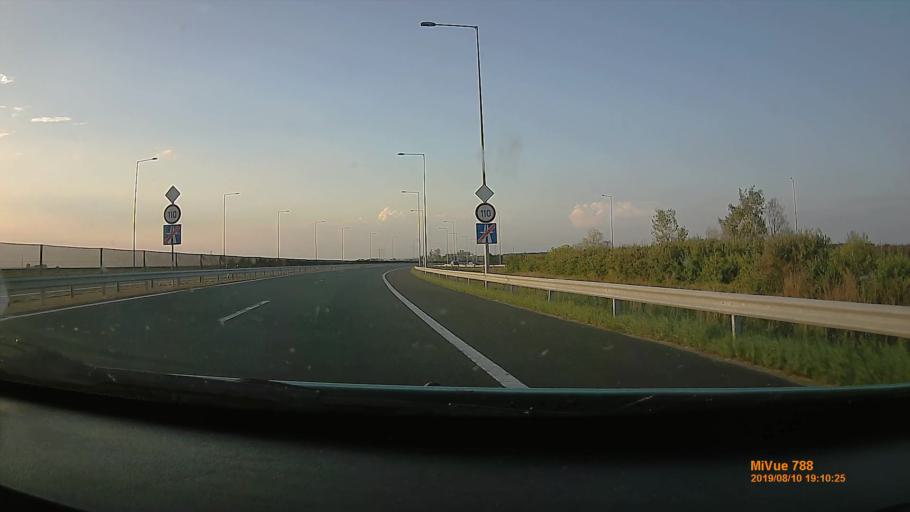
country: HU
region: Borsod-Abauj-Zemplen
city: Alsozsolca
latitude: 48.0618
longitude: 20.8448
